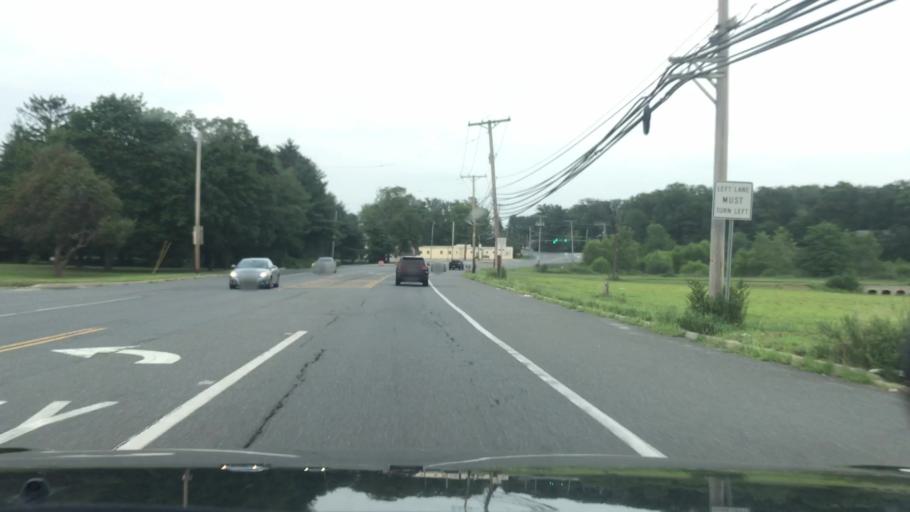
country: US
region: New Jersey
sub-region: Ocean County
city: Lakewood
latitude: 40.0842
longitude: -74.2627
